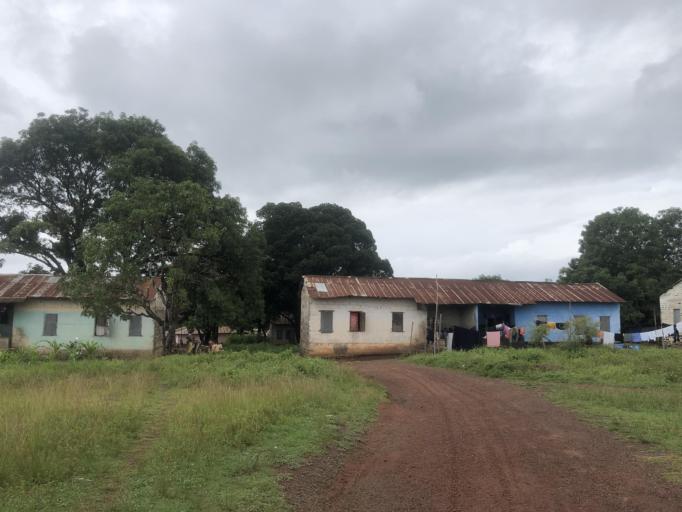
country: SL
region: Northern Province
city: Magburaka
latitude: 8.7188
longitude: -11.9355
